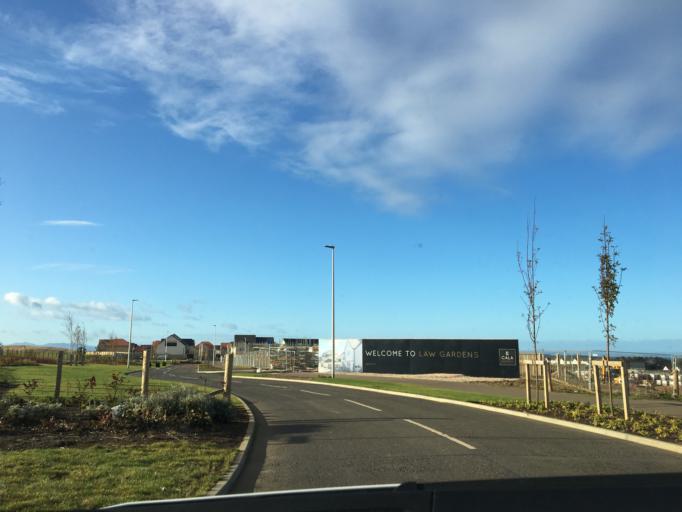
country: GB
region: Scotland
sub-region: East Lothian
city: North Berwick
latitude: 56.0490
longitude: -2.7236
